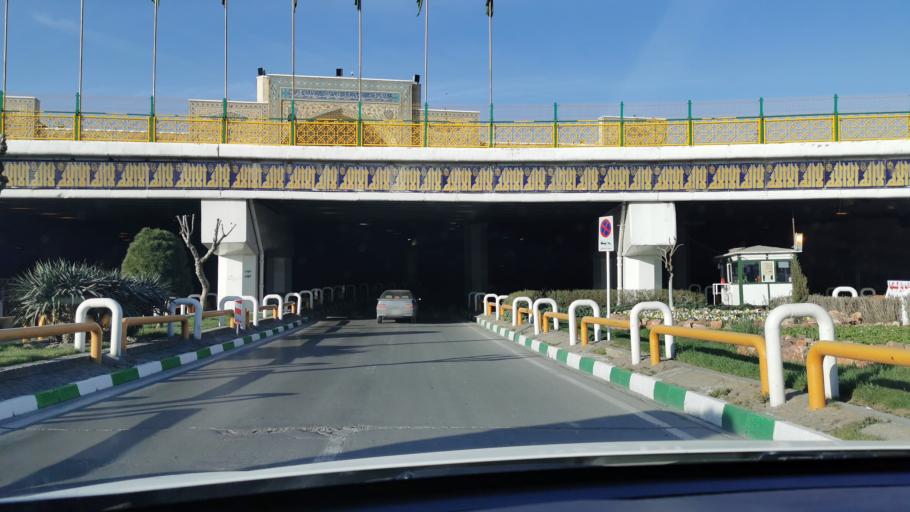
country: IR
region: Razavi Khorasan
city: Mashhad
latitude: 36.2898
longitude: 59.6186
